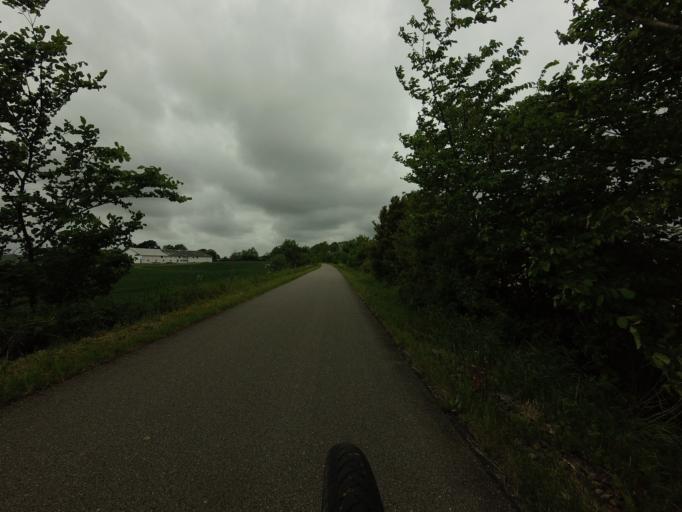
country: DK
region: Zealand
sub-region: Slagelse Kommune
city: Slagelse
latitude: 55.3726
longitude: 11.3813
